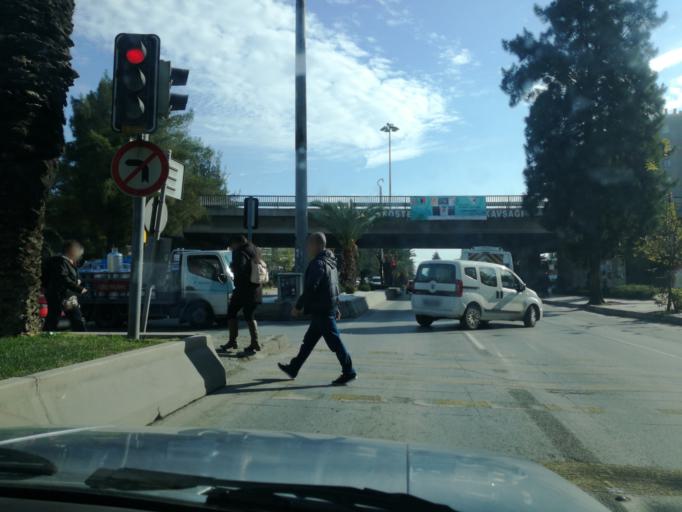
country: TR
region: Izmir
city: Izmir
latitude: 38.3996
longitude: 27.1281
